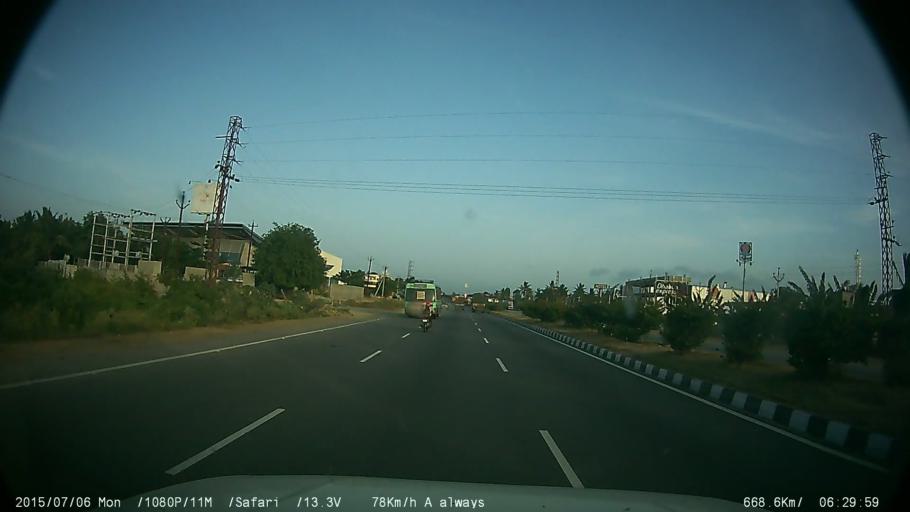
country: IN
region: Tamil Nadu
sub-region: Krishnagiri
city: Kelamangalam
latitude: 12.6792
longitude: 77.9579
